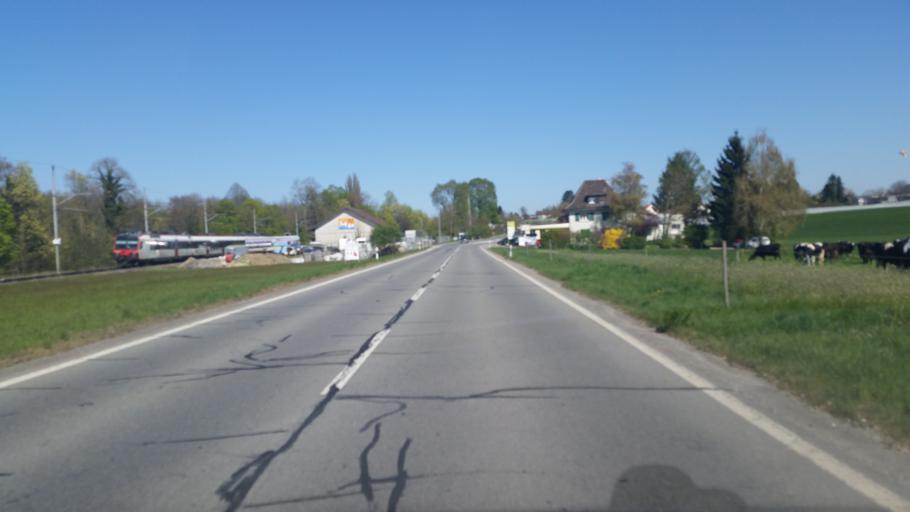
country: CH
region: Fribourg
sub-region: See District
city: Murten
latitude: 46.9250
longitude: 7.1225
